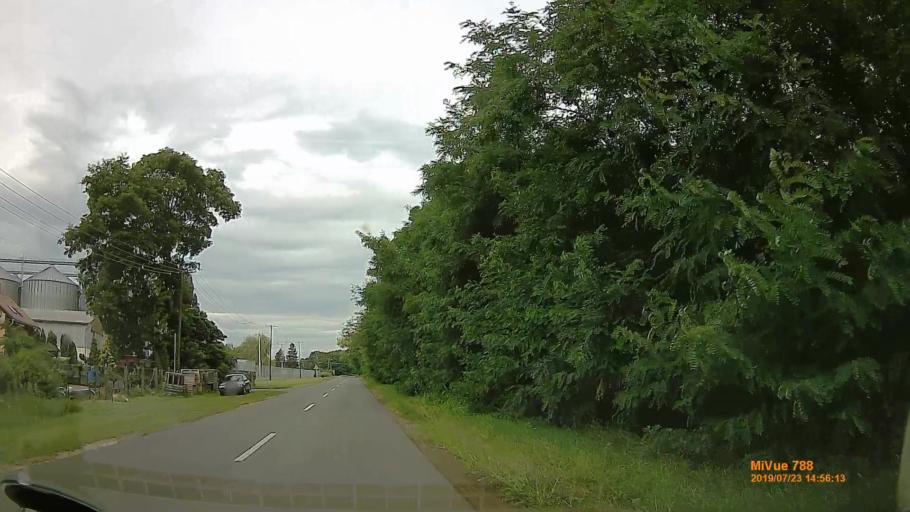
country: HU
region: Szabolcs-Szatmar-Bereg
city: Nyiregyhaza
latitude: 47.8973
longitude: 21.6637
